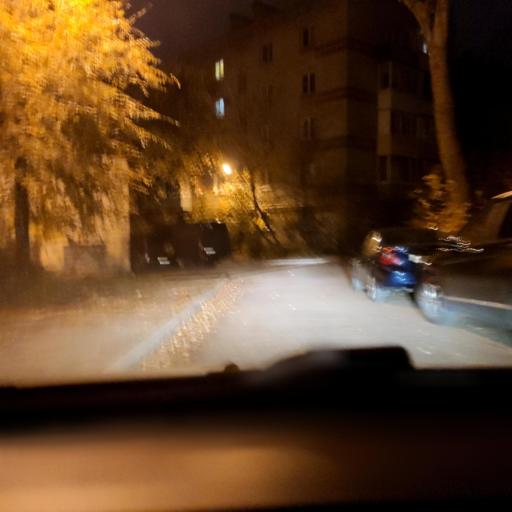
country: RU
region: Voronezj
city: Voronezh
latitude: 51.6464
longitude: 39.1627
